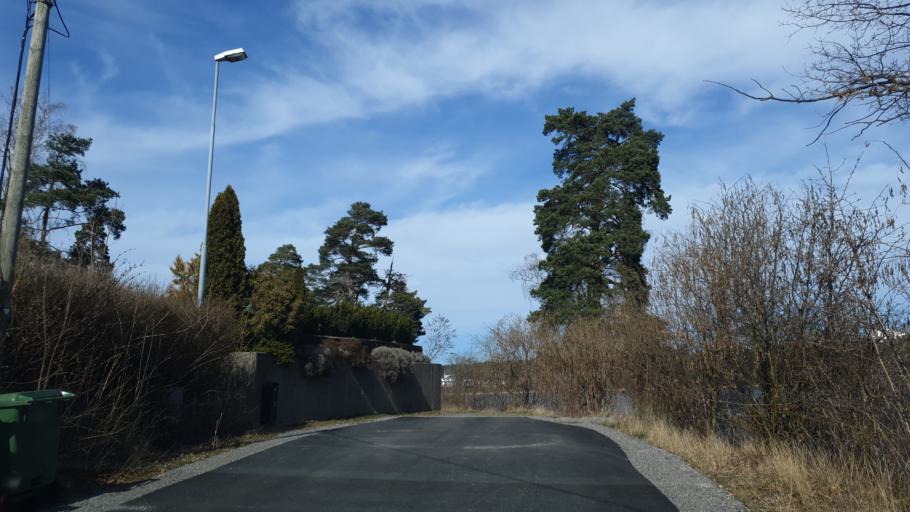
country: SE
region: Stockholm
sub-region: Sollentuna Kommun
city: Sollentuna
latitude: 59.4206
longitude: 17.9816
